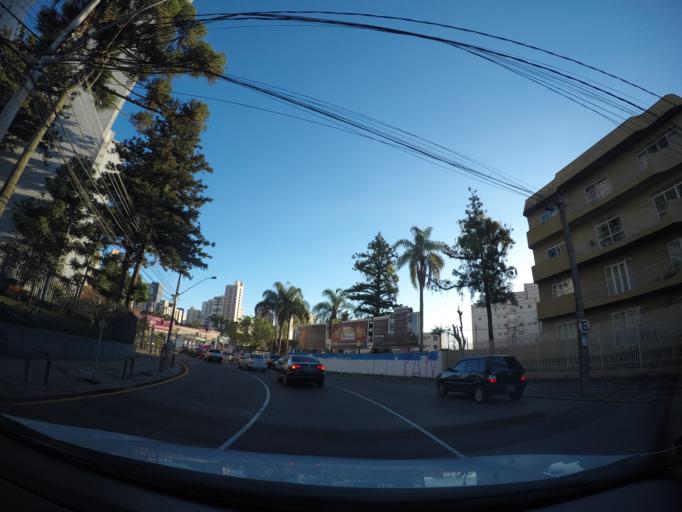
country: BR
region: Parana
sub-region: Curitiba
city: Curitiba
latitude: -25.4120
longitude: -49.2546
